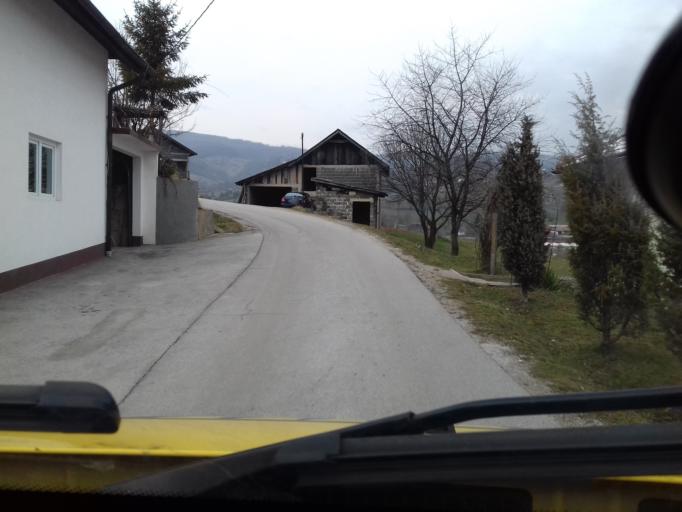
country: BA
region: Federation of Bosnia and Herzegovina
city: Gromiljak
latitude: 44.0173
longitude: 18.0175
